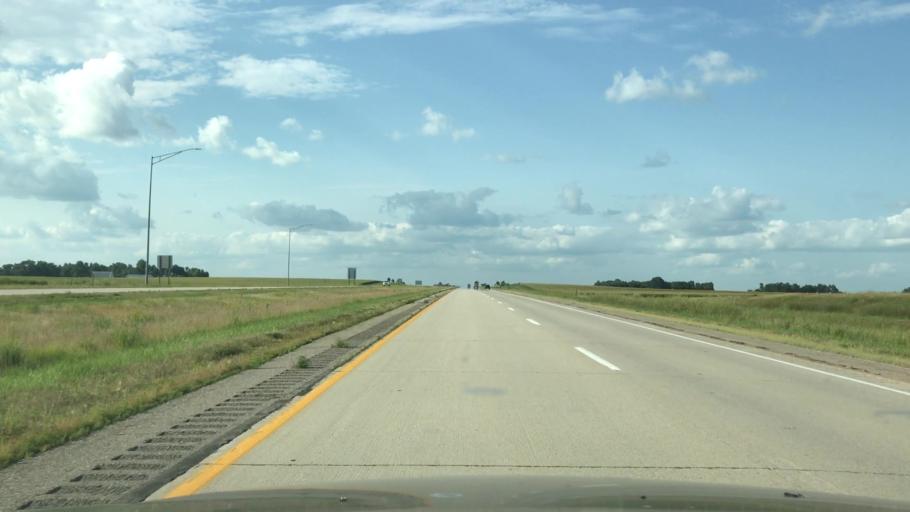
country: US
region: Iowa
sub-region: Osceola County
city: Sibley
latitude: 43.4079
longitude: -95.7170
